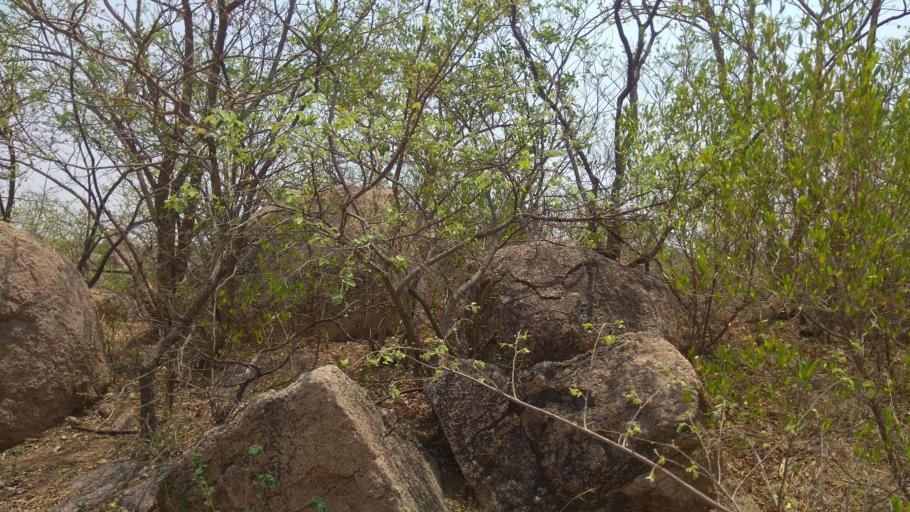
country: IN
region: Telangana
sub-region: Mahbubnagar
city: Farrukhnagar
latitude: 16.8858
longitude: 78.4983
